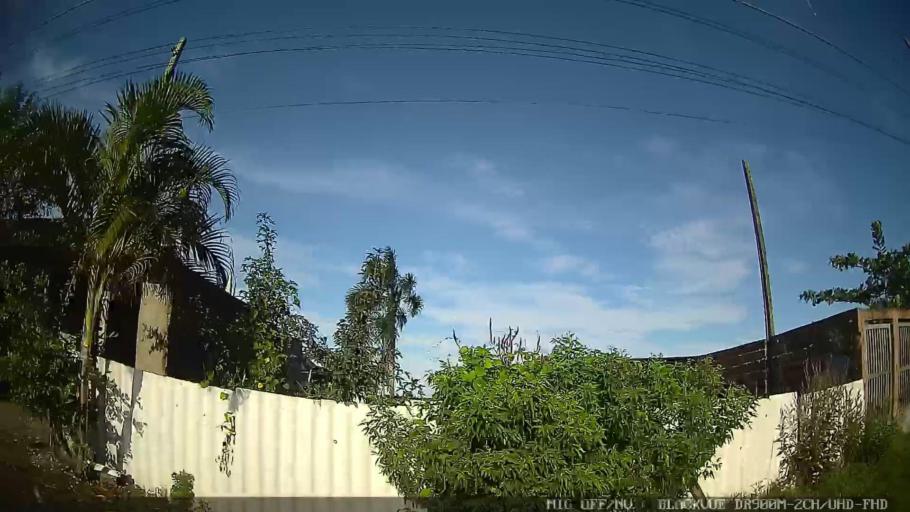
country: BR
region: Sao Paulo
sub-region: Iguape
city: Iguape
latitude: -24.7553
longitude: -47.5751
